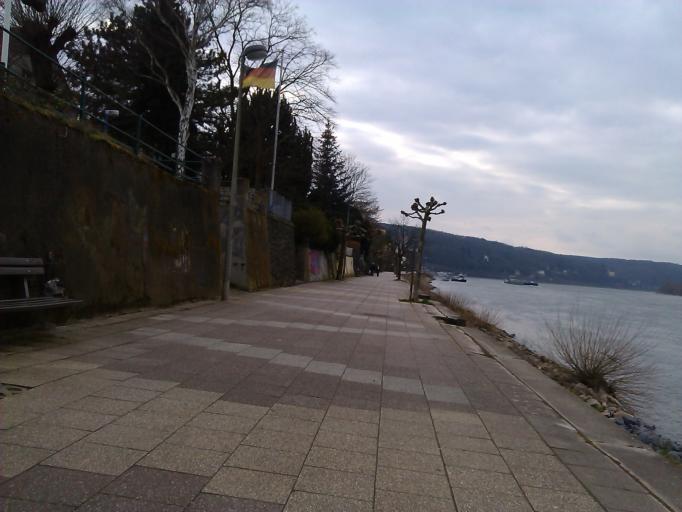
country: DE
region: Rheinland-Pfalz
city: Erpel
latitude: 50.5784
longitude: 7.2409
